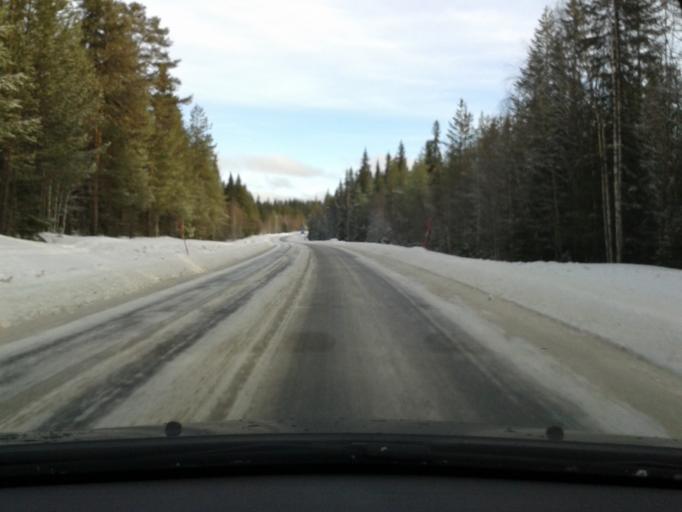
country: SE
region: Vaesterbotten
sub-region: Vilhelmina Kommun
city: Vilhelmina
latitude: 64.6478
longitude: 16.5670
